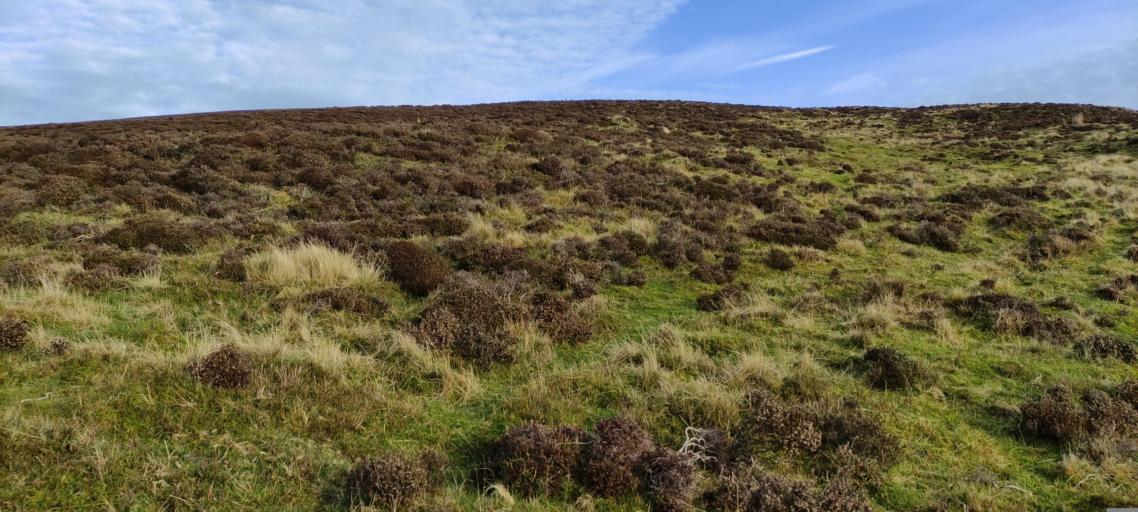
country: GB
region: England
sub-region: Cumbria
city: Millom
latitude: 54.2471
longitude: -3.3325
